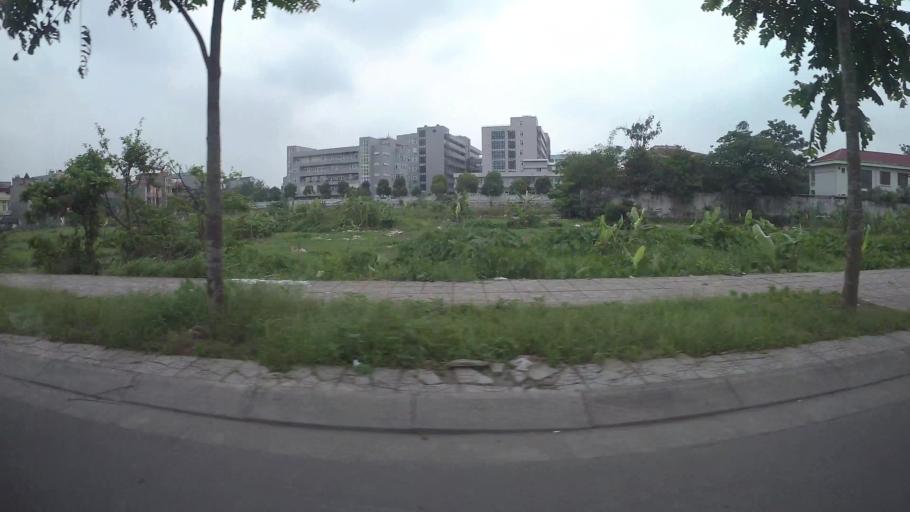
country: VN
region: Ha Noi
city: Trau Quy
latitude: 21.0617
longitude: 105.9003
